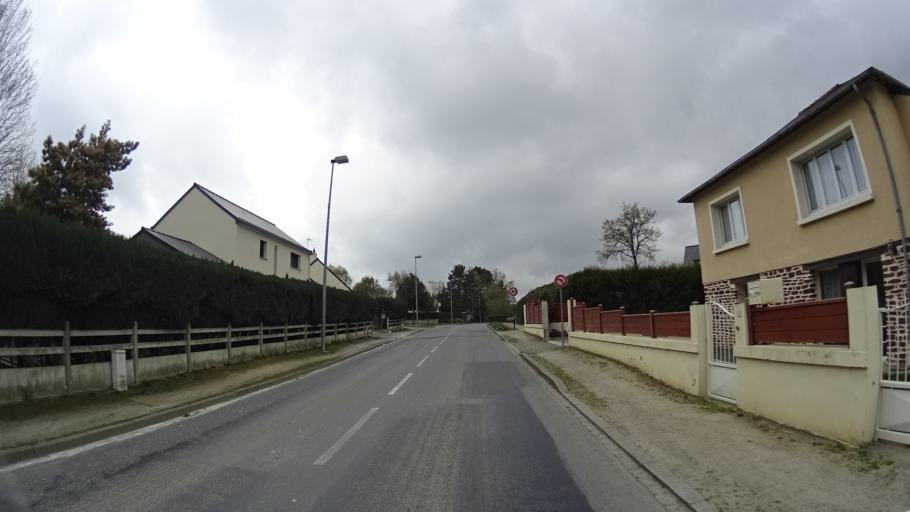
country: FR
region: Brittany
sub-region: Departement d'Ille-et-Vilaine
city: Cintre
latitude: 48.1025
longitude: -1.8686
